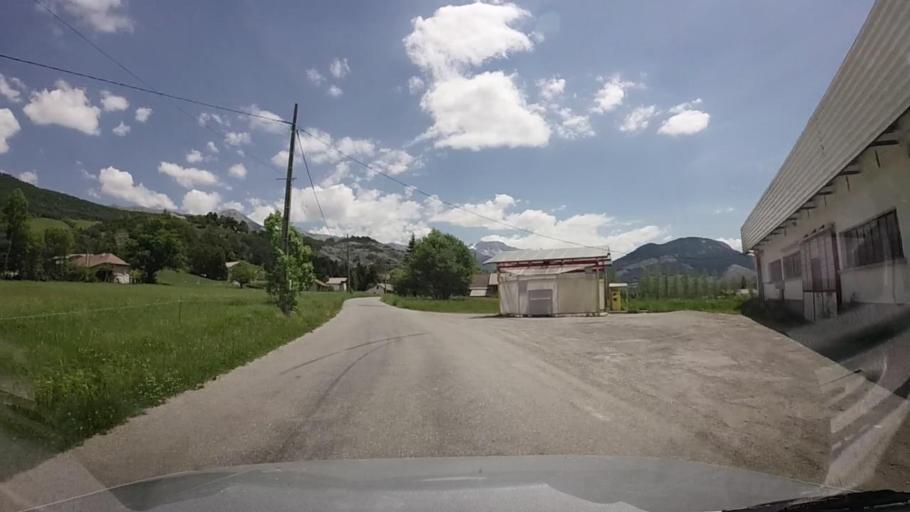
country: FR
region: Provence-Alpes-Cote d'Azur
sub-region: Departement des Alpes-de-Haute-Provence
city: Seyne-les-Alpes
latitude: 44.3553
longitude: 6.3393
